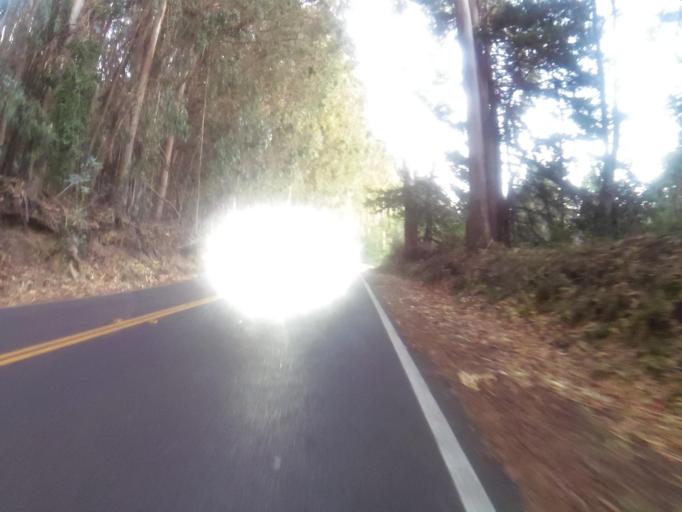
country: US
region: California
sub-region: Sonoma County
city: Sea Ranch
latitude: 38.5982
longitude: -123.3486
